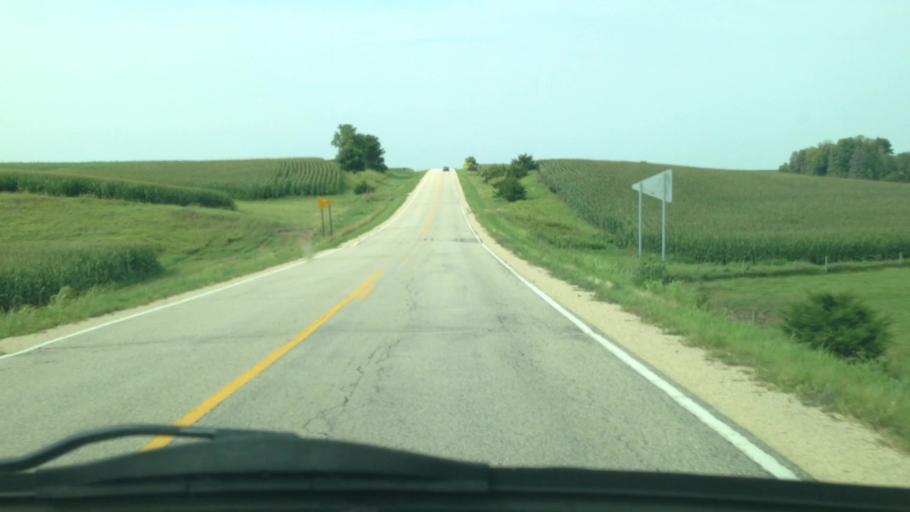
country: US
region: Minnesota
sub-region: Winona County
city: Saint Charles
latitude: 43.8659
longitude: -91.9593
